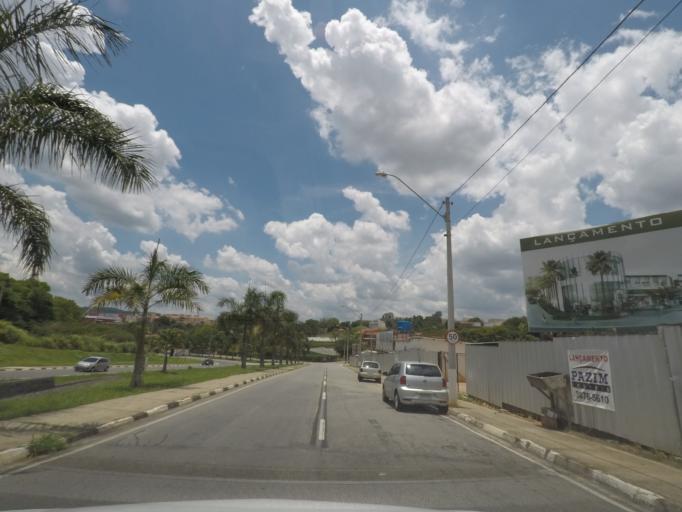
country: BR
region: Sao Paulo
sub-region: Vinhedo
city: Vinhedo
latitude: -23.0398
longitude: -46.9825
